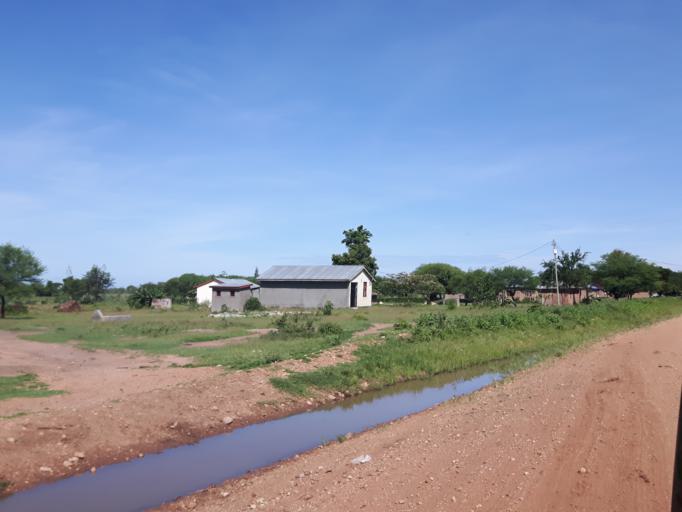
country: TZ
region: Mara
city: Issenye
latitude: -1.9614
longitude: 34.2725
